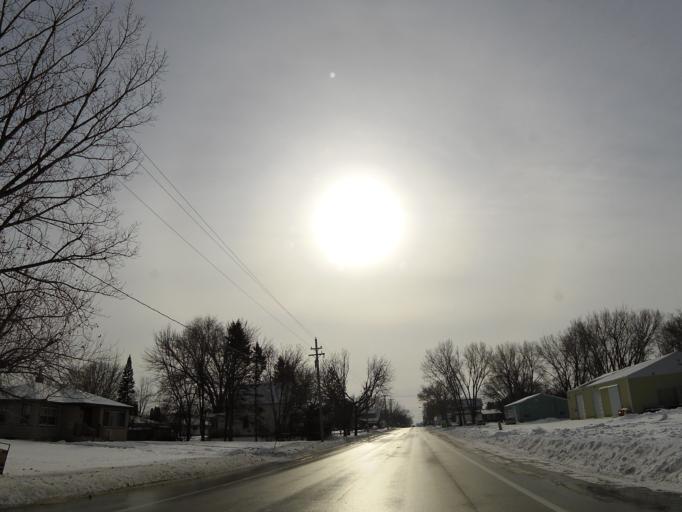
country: US
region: Minnesota
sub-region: McLeod County
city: Lester Prairie
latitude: 44.8864
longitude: -93.9704
